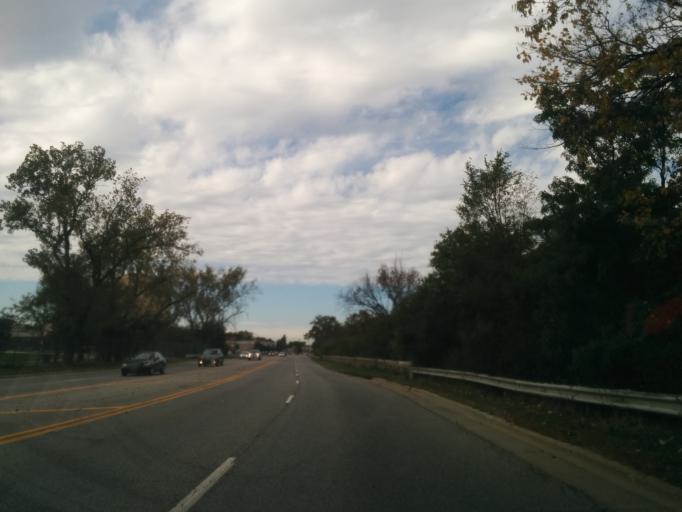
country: US
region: Illinois
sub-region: Cook County
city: Schiller Park
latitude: 41.9544
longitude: -87.8572
